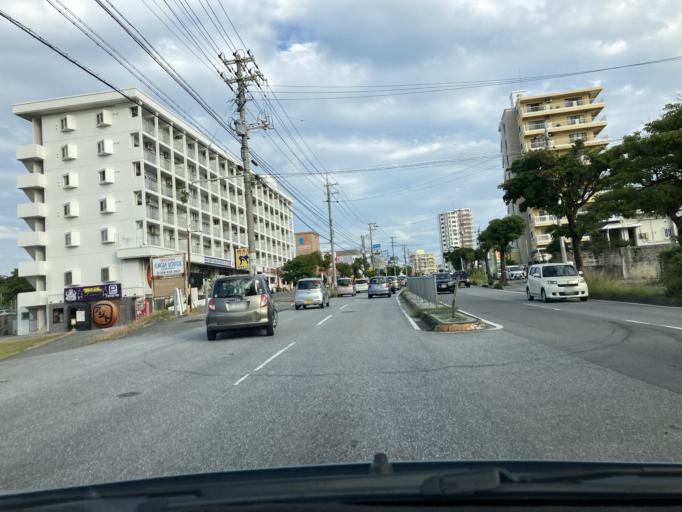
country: JP
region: Okinawa
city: Chatan
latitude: 26.3277
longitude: 127.7620
